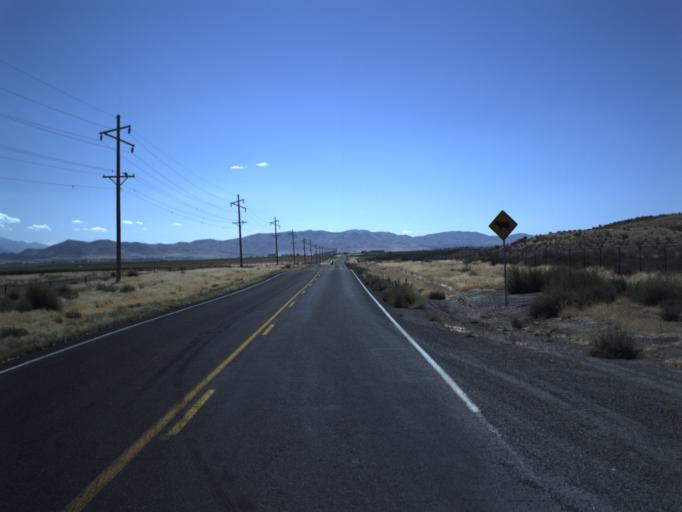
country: US
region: Utah
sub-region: Utah County
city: Genola
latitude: 40.0336
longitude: -111.9584
